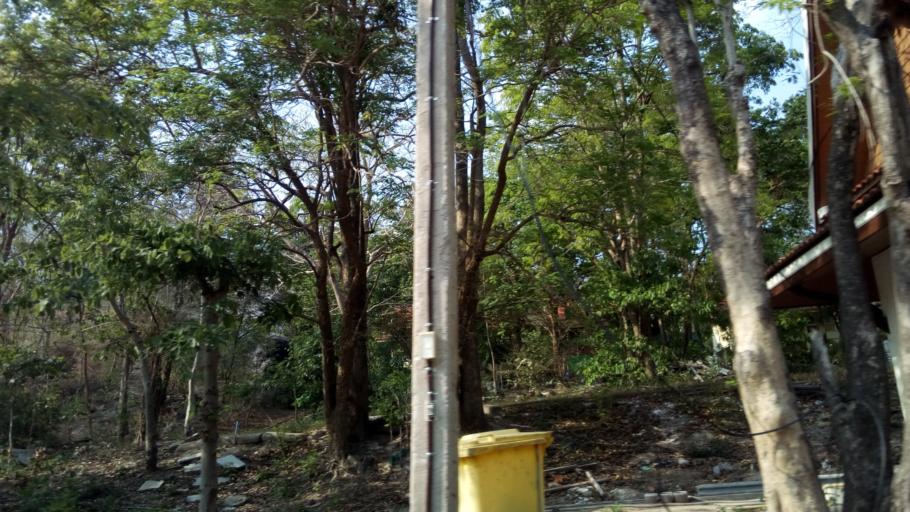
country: TH
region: Sara Buri
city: Saraburi
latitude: 14.4608
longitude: 100.9463
